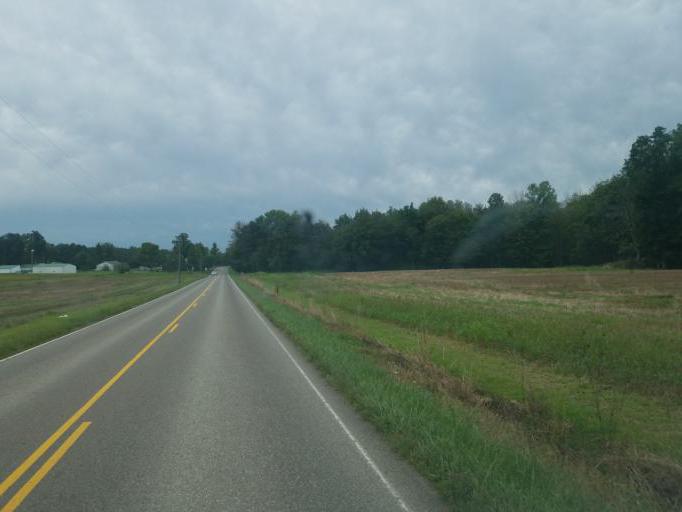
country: US
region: Ohio
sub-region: Knox County
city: Fredericktown
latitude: 40.5289
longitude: -82.5998
